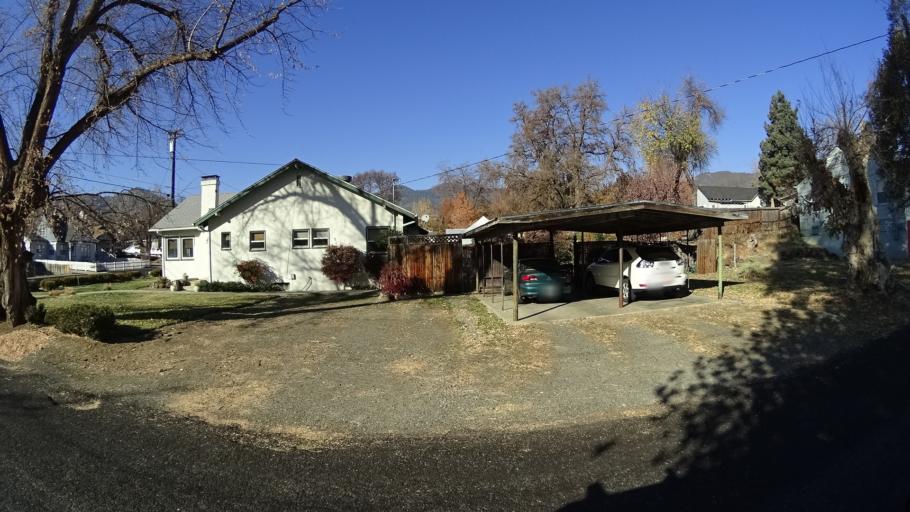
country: US
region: California
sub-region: Siskiyou County
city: Yreka
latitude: 41.7336
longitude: -122.6436
